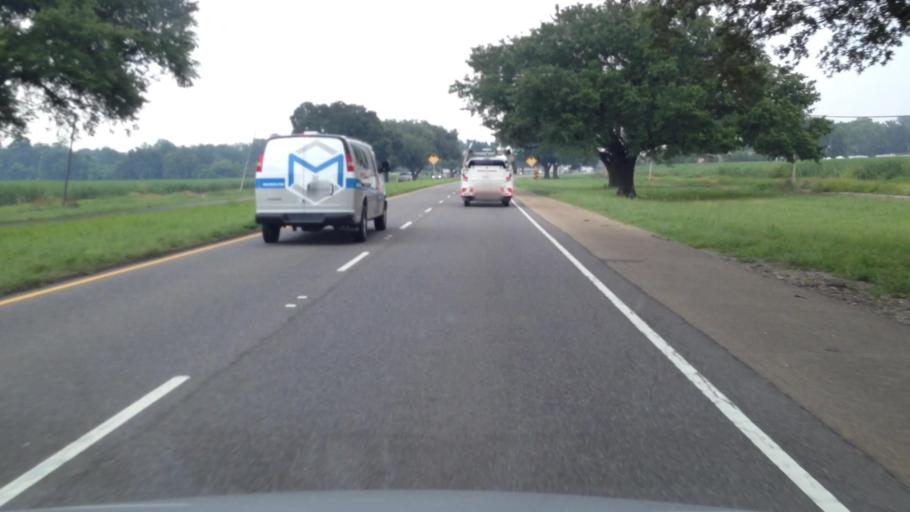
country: US
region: Louisiana
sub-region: West Baton Rouge Parish
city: Port Allen
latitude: 30.5033
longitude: -91.2324
